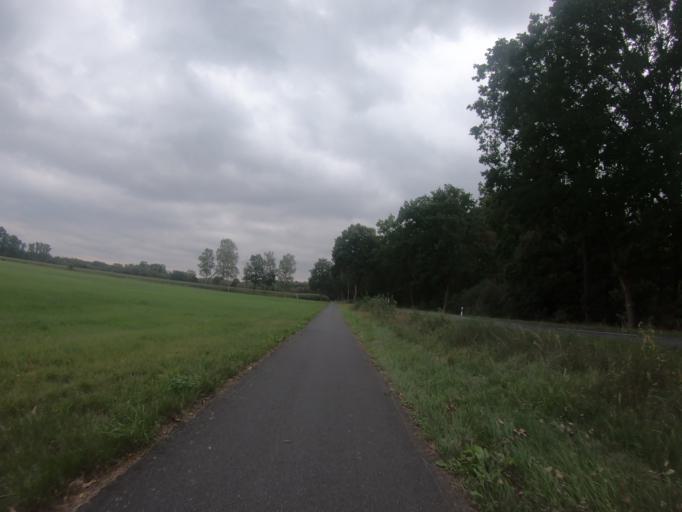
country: DE
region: Lower Saxony
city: Ribbesbuttel
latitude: 52.4484
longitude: 10.5004
